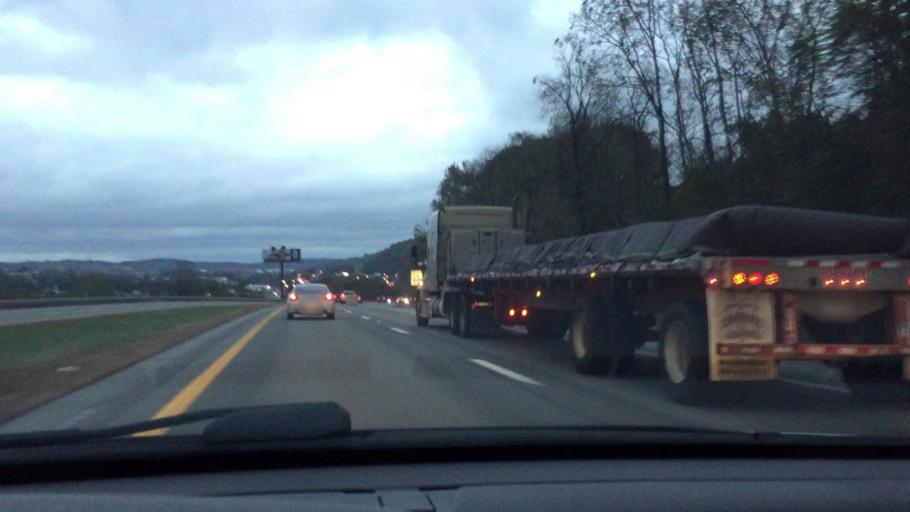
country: US
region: Pennsylvania
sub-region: Washington County
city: Canonsburg
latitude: 40.2504
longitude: -80.1911
